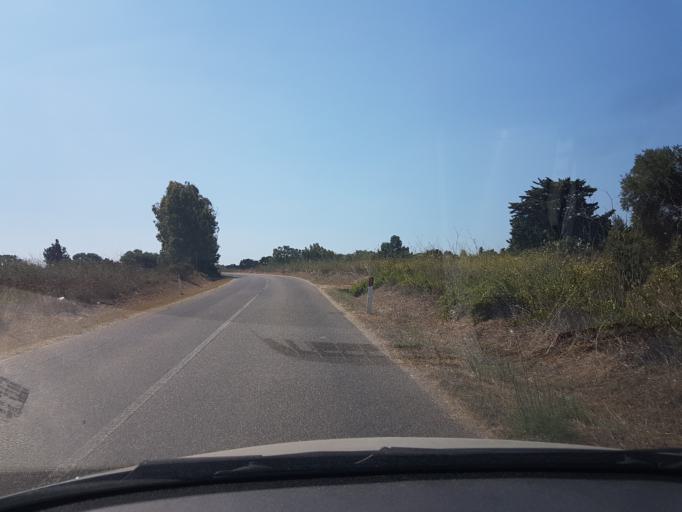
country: IT
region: Sardinia
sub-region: Provincia di Oristano
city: Riola Sardo
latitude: 39.9983
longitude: 8.4904
